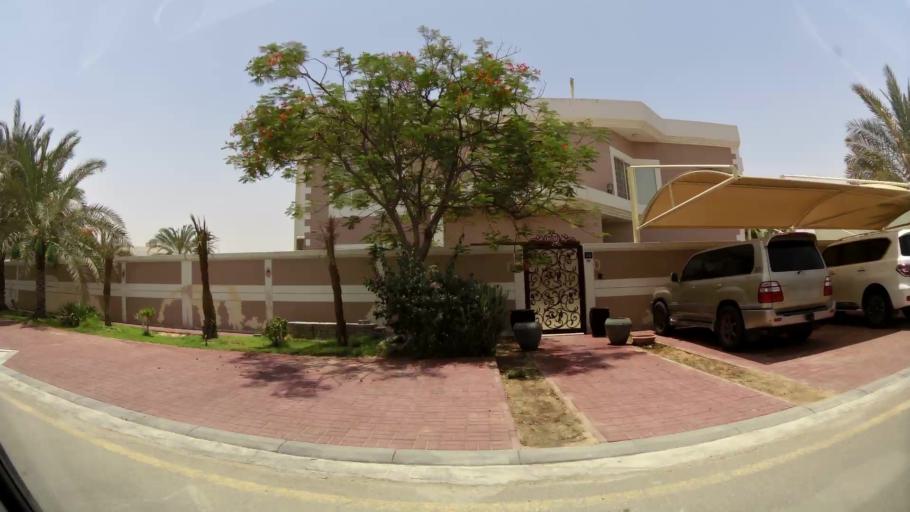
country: AE
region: Ash Shariqah
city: Sharjah
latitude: 25.2400
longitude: 55.4597
